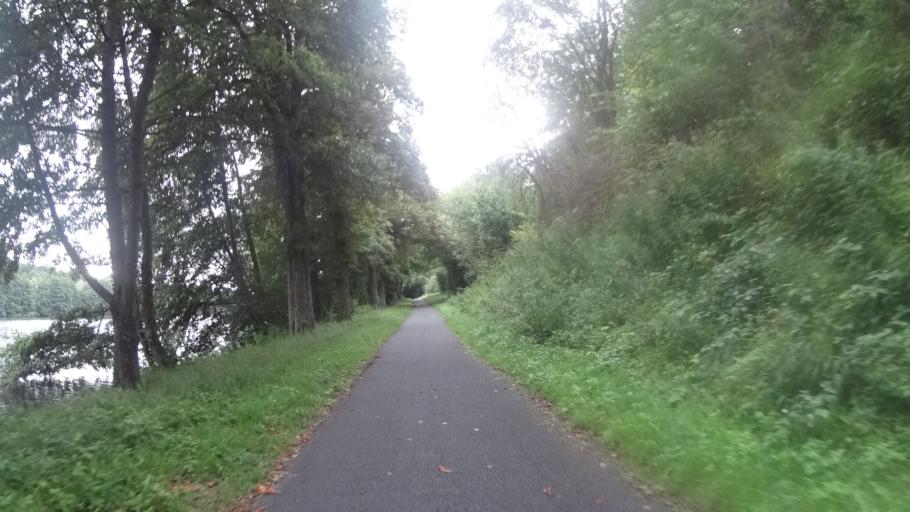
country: FR
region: Lorraine
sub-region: Departement de Meurthe-et-Moselle
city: Gondreville
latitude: 48.6506
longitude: 5.9858
